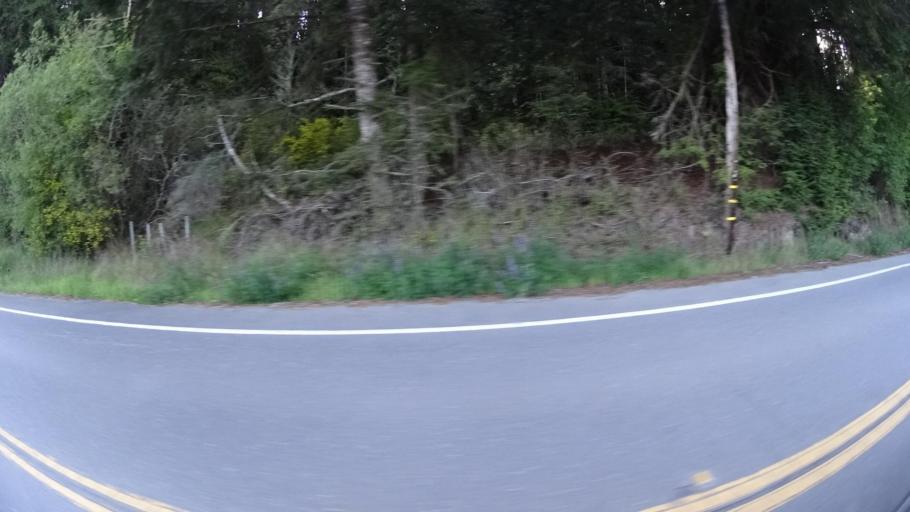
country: US
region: California
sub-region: Humboldt County
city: Bayside
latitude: 40.7591
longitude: -124.0511
